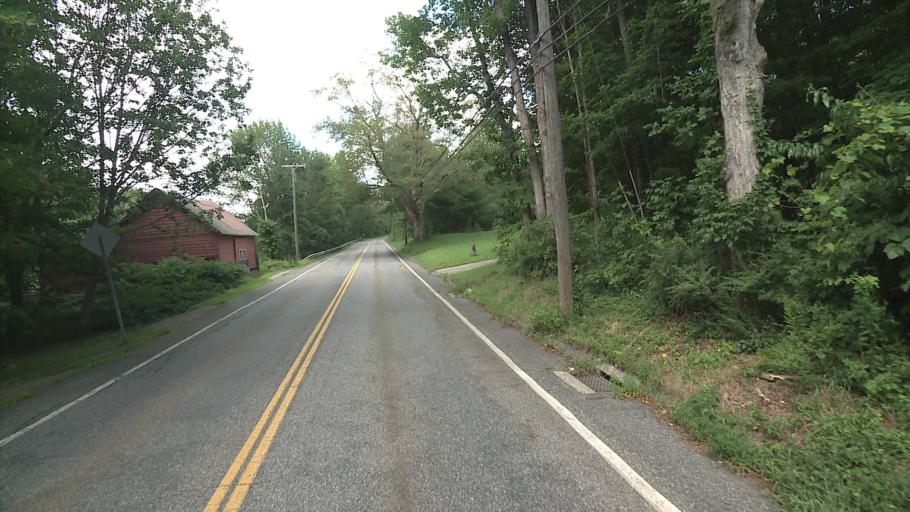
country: US
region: Connecticut
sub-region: Tolland County
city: Storrs
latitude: 41.9077
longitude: -72.1720
